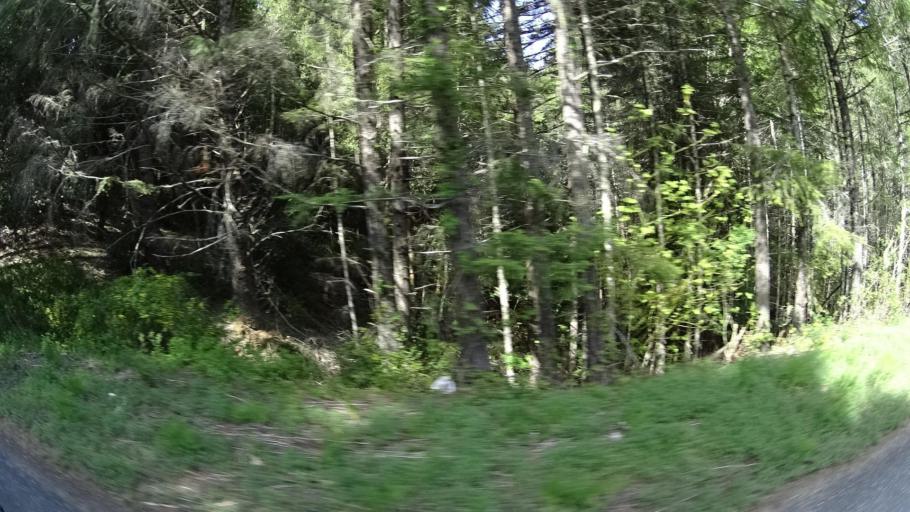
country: US
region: California
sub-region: Humboldt County
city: Redway
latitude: 40.4379
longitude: -123.7789
